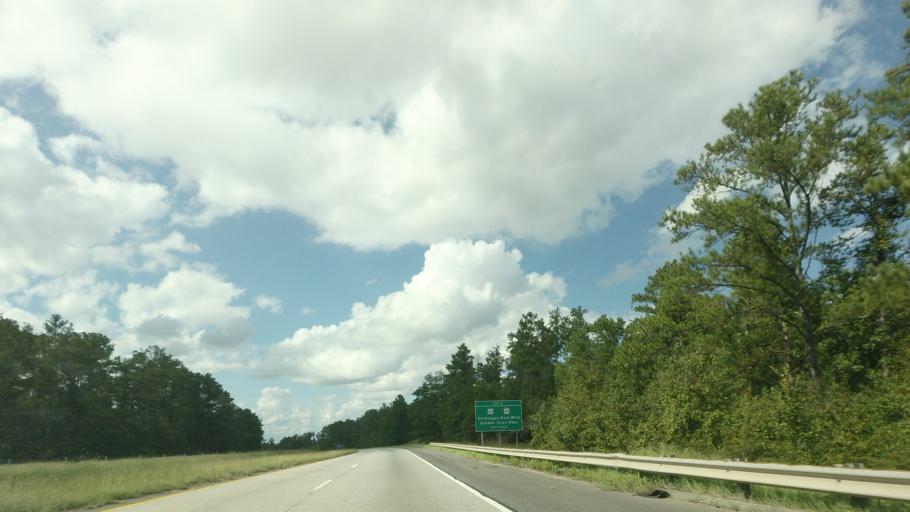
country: US
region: Georgia
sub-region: Bibb County
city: Macon
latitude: 32.7835
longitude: -83.5590
